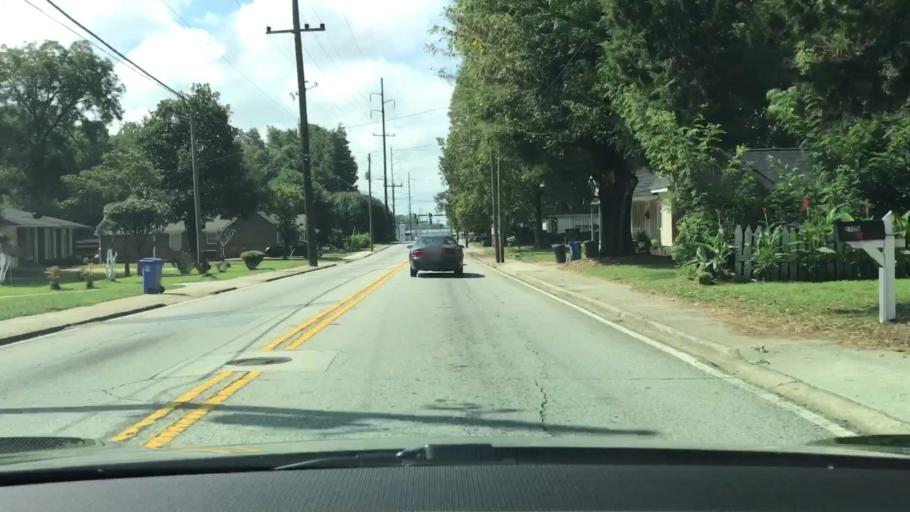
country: US
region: Georgia
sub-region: Hall County
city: Gainesville
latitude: 34.2963
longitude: -83.8146
